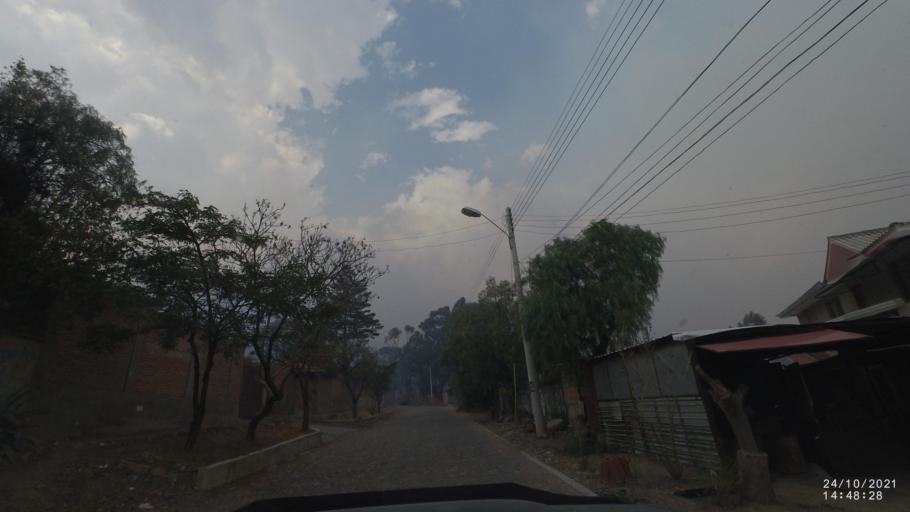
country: BO
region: Cochabamba
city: Cochabamba
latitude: -17.3511
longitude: -66.1508
